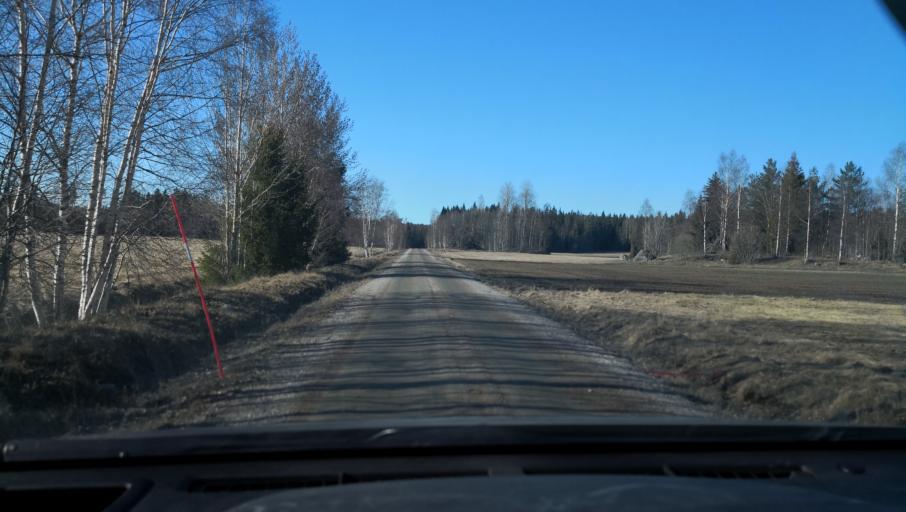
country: SE
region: Vaestmanland
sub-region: Sala Kommun
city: Sala
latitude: 60.1309
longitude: 16.6523
